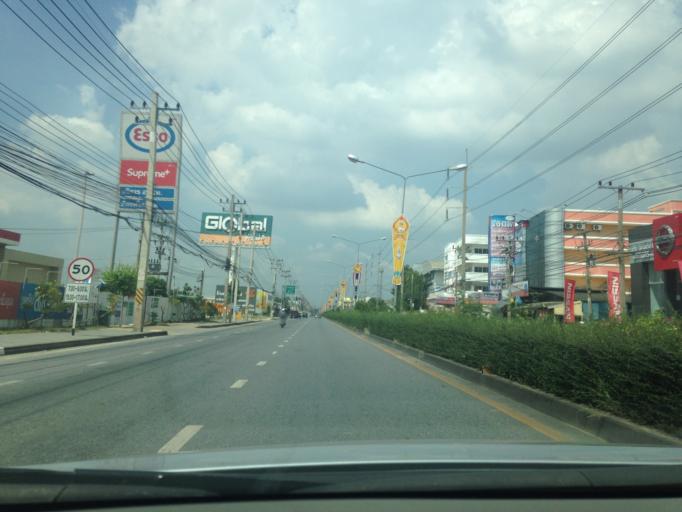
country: TH
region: Pathum Thani
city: Pathum Thani
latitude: 14.0345
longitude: 100.5252
